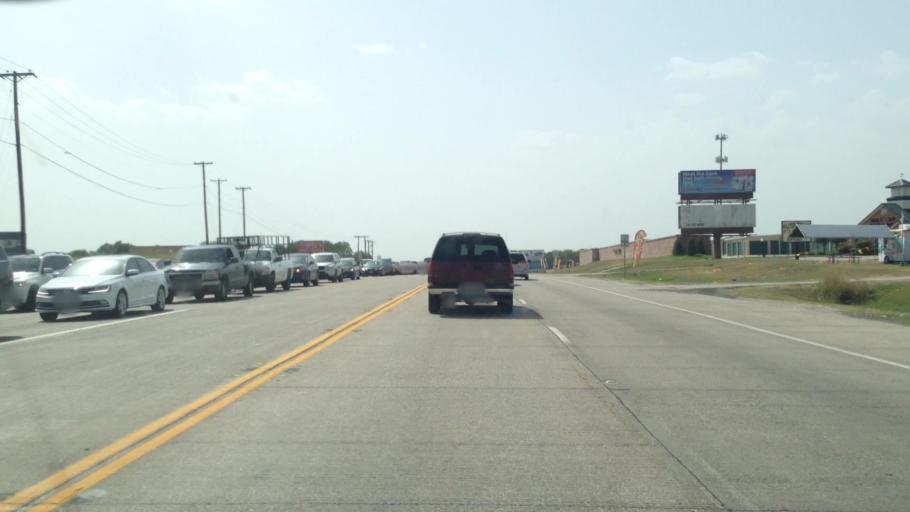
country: US
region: Texas
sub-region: Collin County
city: Lowry Crossing
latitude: 33.1898
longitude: -96.5481
